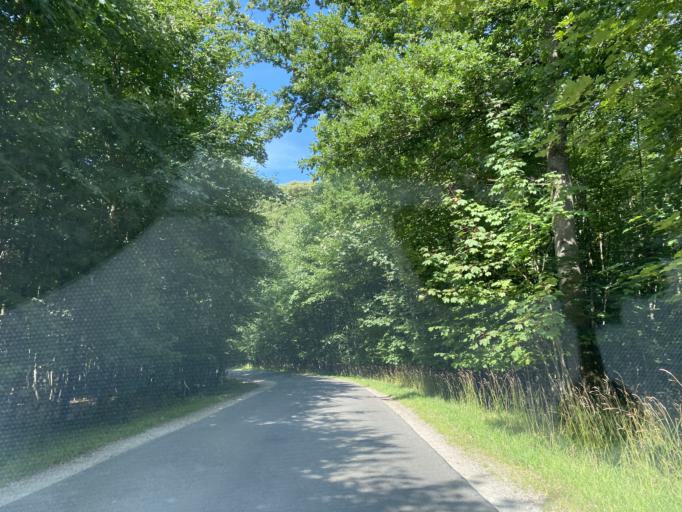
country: DK
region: Central Jutland
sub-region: Favrskov Kommune
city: Hammel
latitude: 56.2535
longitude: 9.8179
